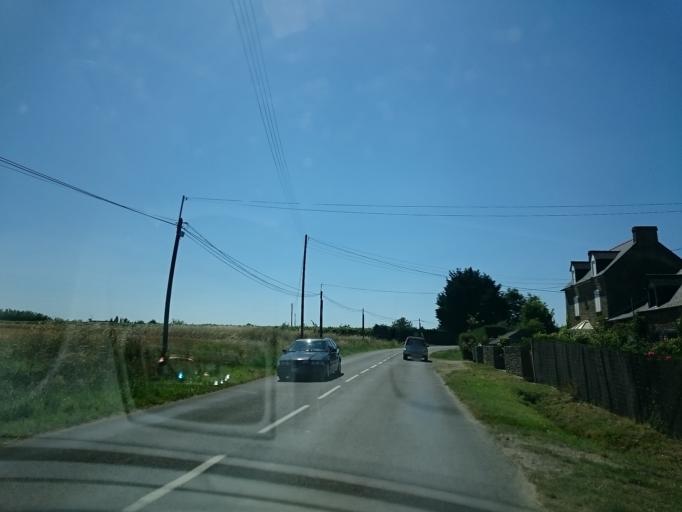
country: FR
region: Brittany
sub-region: Departement d'Ille-et-Vilaine
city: Saint-Coulomb
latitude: 48.6888
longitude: -1.9157
